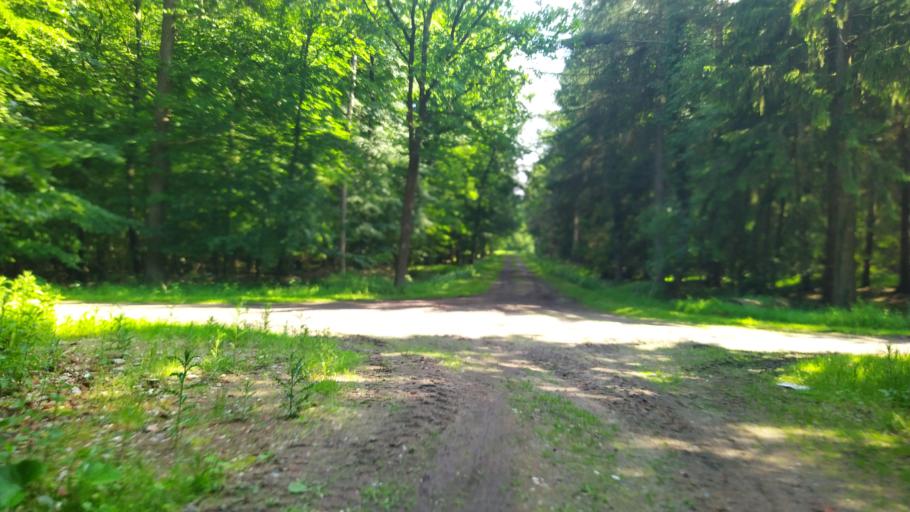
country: DE
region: Lower Saxony
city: Wohnste
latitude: 53.3916
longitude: 9.5154
